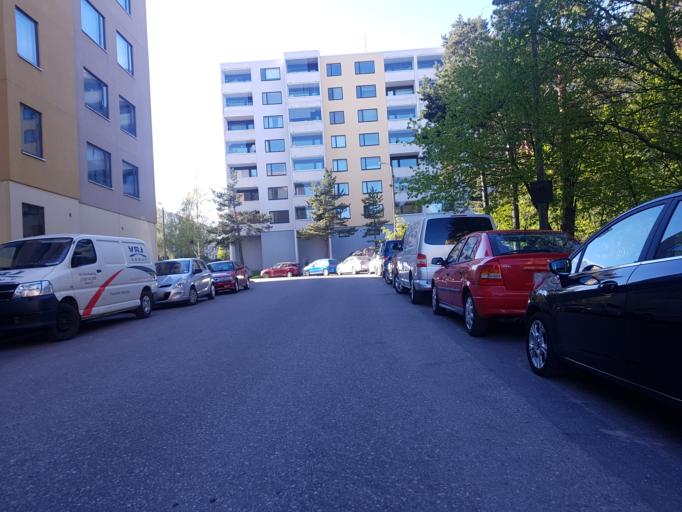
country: FI
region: Uusimaa
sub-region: Helsinki
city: Vantaa
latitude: 60.2321
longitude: 24.9999
